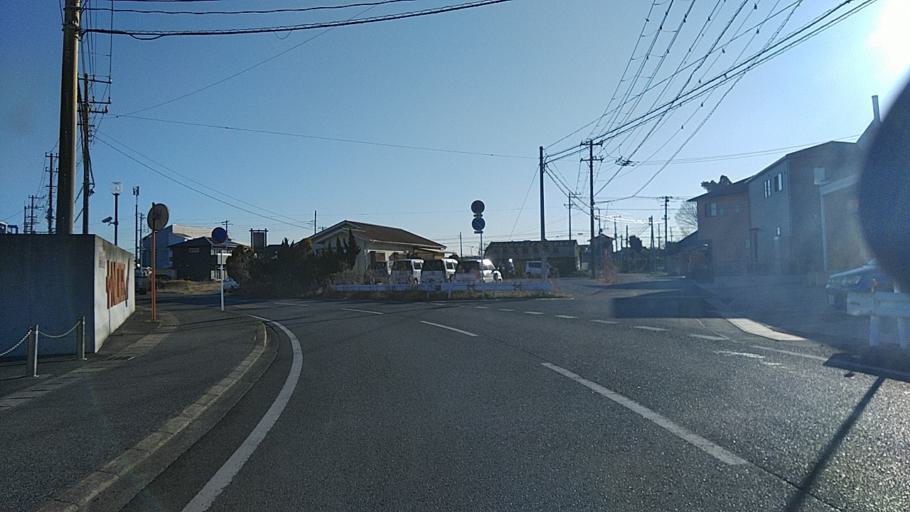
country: JP
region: Chiba
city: Kimitsu
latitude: 35.3197
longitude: 139.8891
